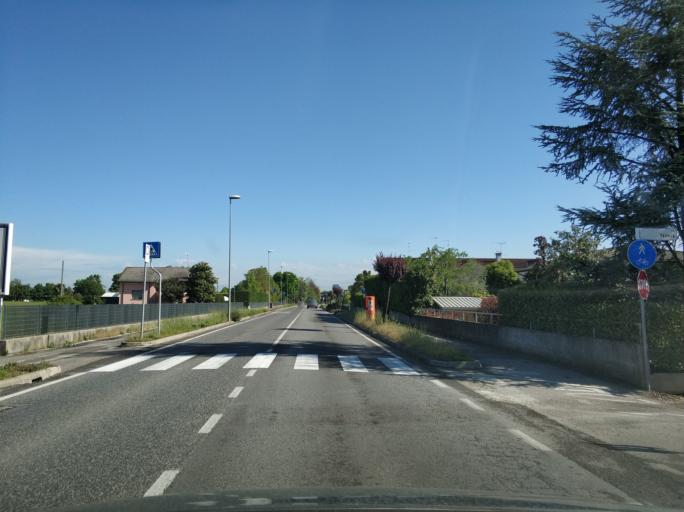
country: IT
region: Friuli Venezia Giulia
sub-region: Provincia di Udine
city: Porpetto
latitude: 45.8510
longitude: 13.2133
